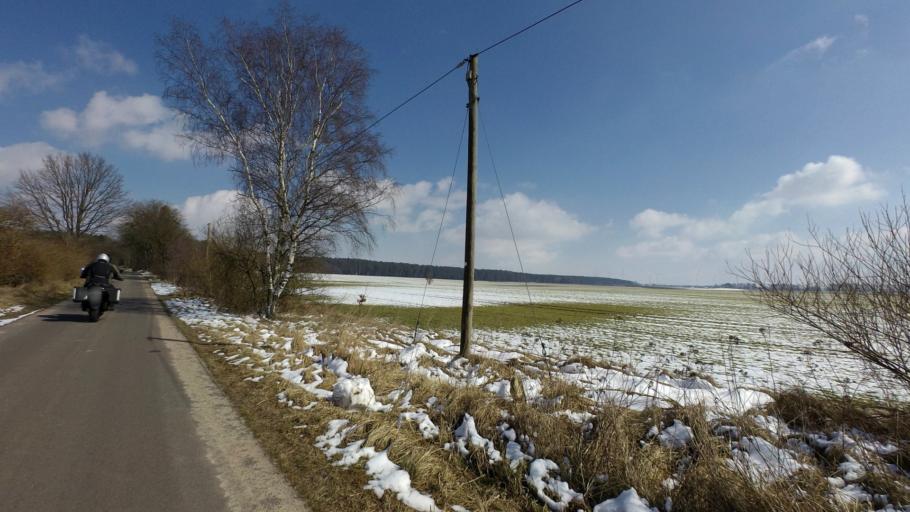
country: DE
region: Brandenburg
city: Werftpfuhl
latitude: 52.7009
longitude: 13.7820
